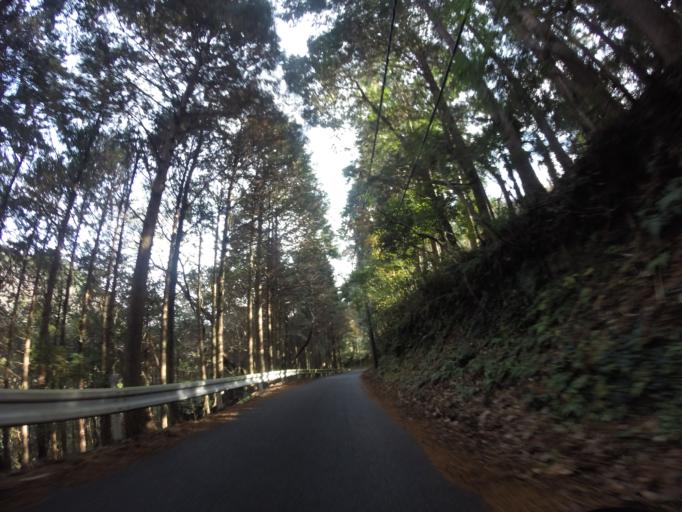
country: JP
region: Shizuoka
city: Heda
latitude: 34.8275
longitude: 138.8415
